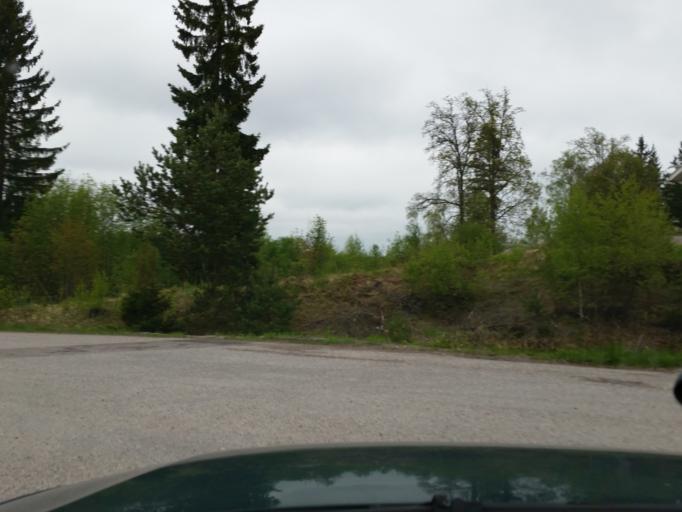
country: FI
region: Uusimaa
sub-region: Helsinki
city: Karjalohja
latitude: 60.1406
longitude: 23.8511
